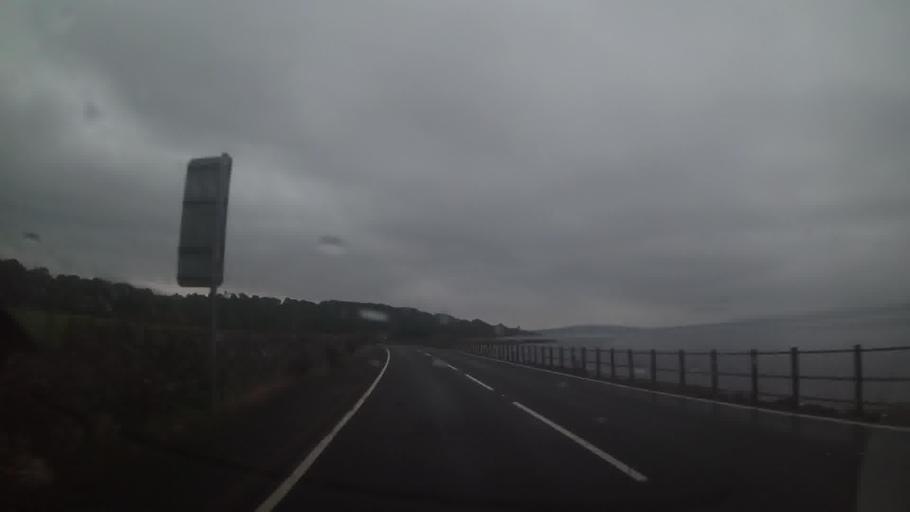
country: GB
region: Scotland
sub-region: North Ayrshire
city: Skelmorlie
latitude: 55.8528
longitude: -4.8890
